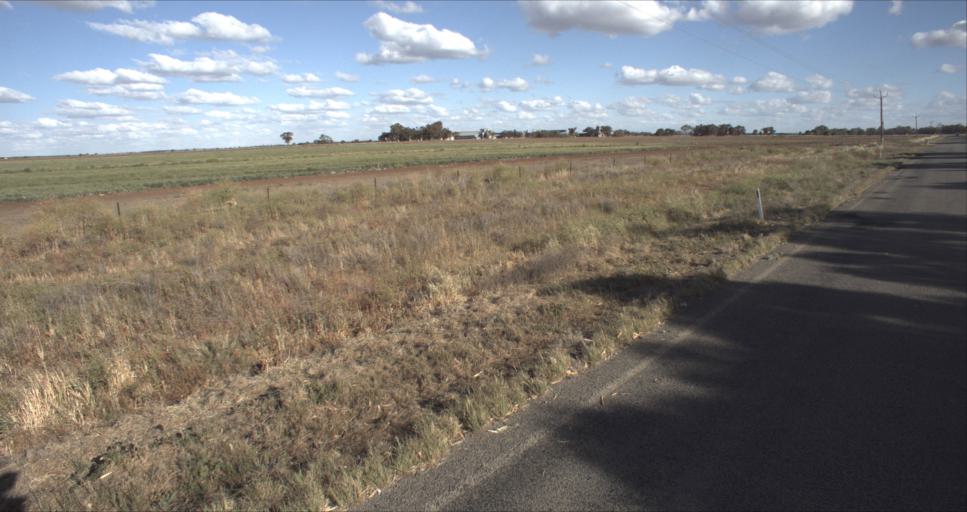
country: AU
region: New South Wales
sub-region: Leeton
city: Leeton
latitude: -34.5480
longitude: 146.2793
